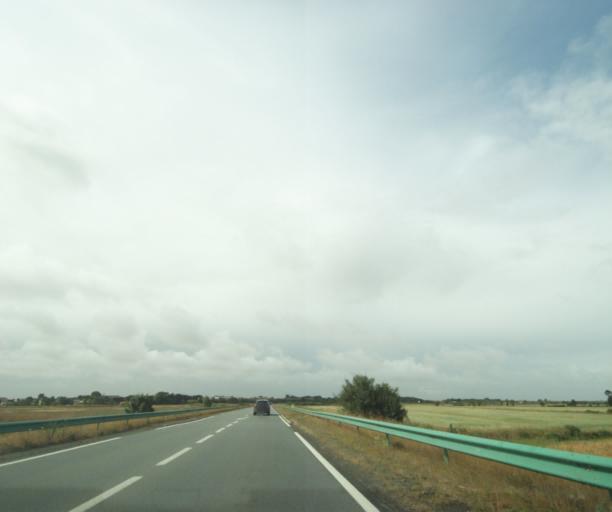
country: FR
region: Poitou-Charentes
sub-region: Departement de la Charente-Maritime
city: Andilly
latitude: 46.2500
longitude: -1.0681
